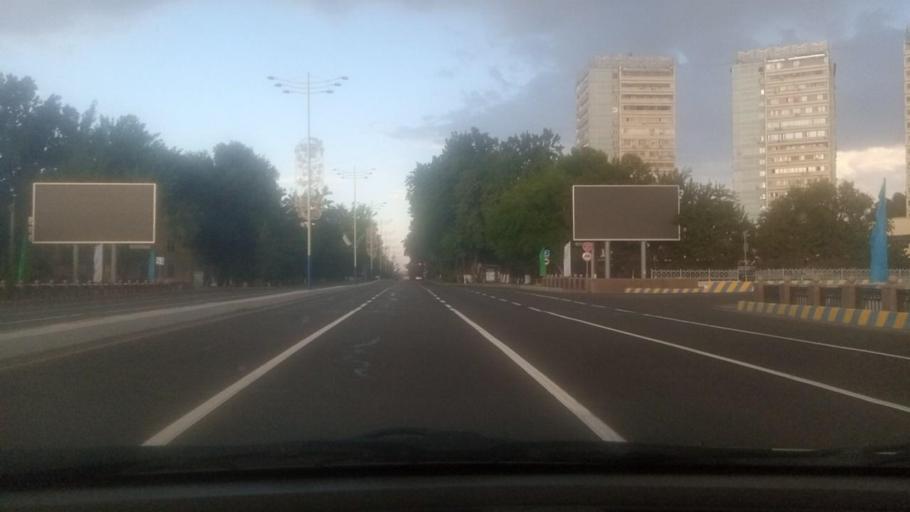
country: UZ
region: Toshkent Shahri
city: Tashkent
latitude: 41.3171
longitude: 69.2931
